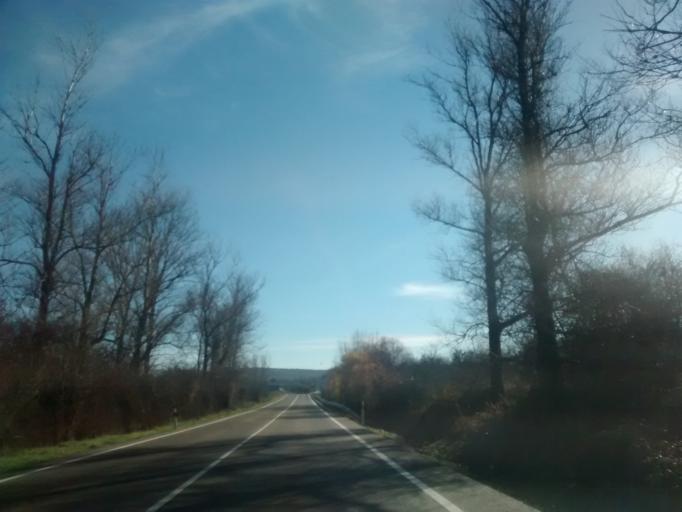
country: ES
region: Cantabria
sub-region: Provincia de Cantabria
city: San Pedro del Romeral
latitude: 42.9761
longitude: -3.7989
